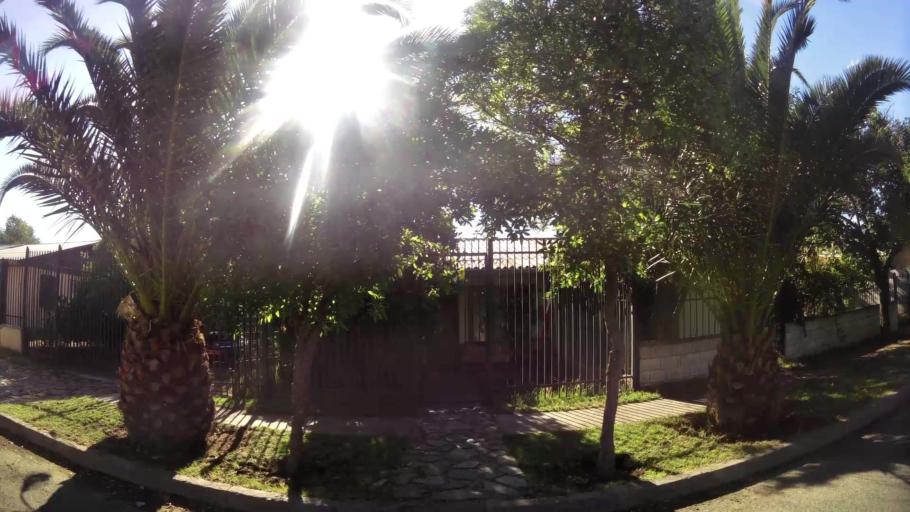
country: CL
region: Santiago Metropolitan
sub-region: Provincia de Chacabuco
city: Lampa
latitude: -33.3965
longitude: -71.1227
